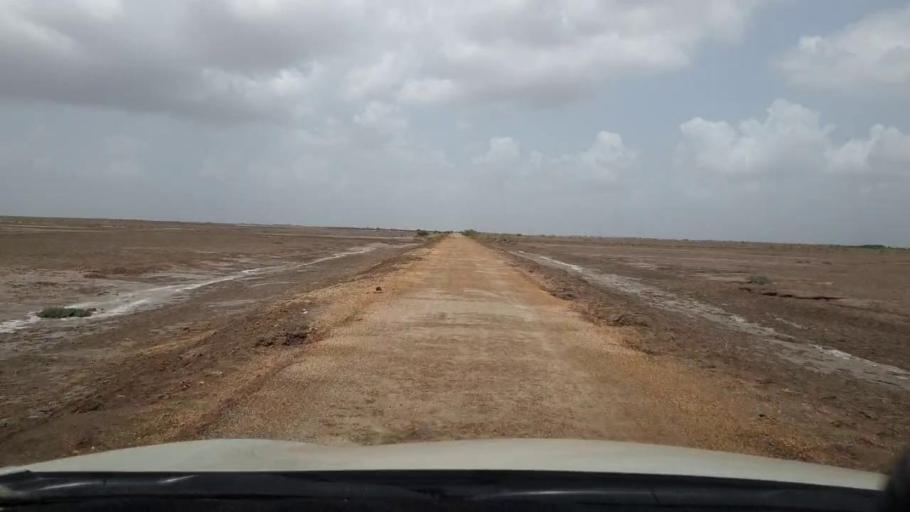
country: PK
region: Sindh
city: Kadhan
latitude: 24.3604
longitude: 68.8431
